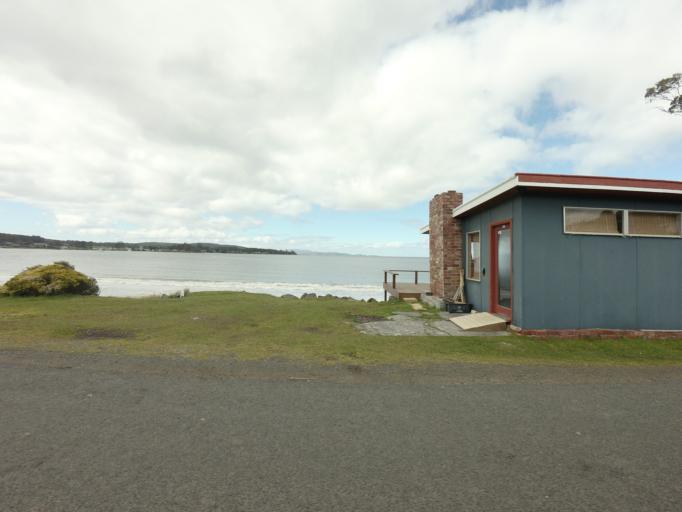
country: AU
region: Tasmania
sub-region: Huon Valley
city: Geeveston
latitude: -43.4376
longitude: 146.9622
